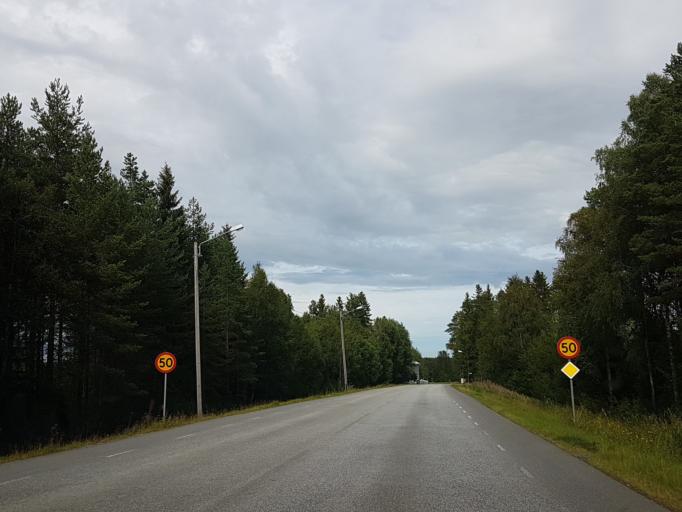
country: SE
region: Vaesterbotten
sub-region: Umea Kommun
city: Taftea
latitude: 63.8348
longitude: 20.4733
